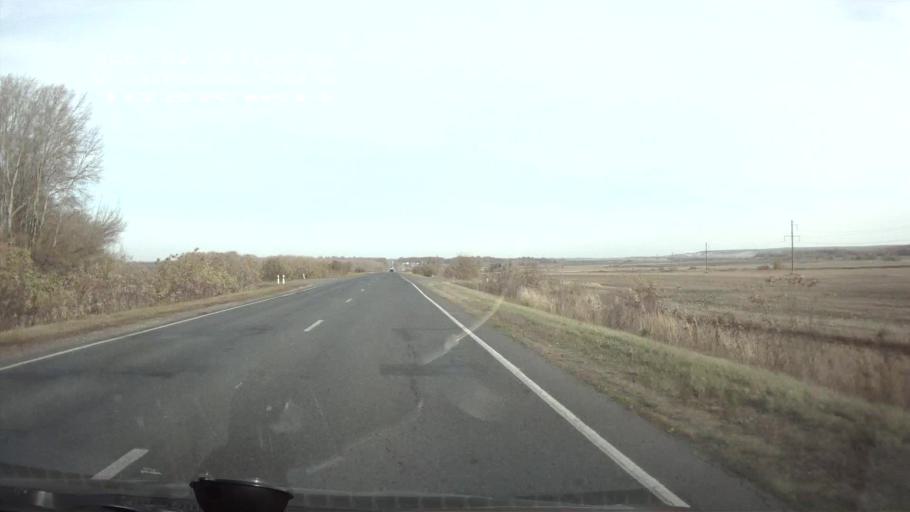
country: RU
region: Mordoviya
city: Atyashevo
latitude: 54.5454
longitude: 45.9472
